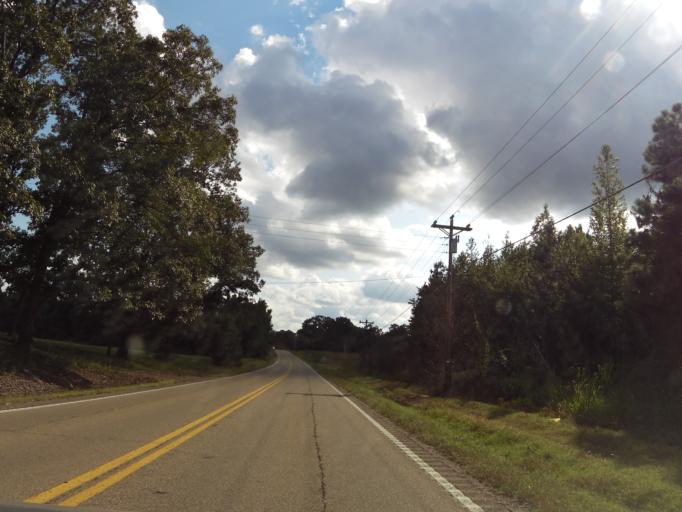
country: US
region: Mississippi
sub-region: Alcorn County
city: Farmington
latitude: 35.0256
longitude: -88.4531
